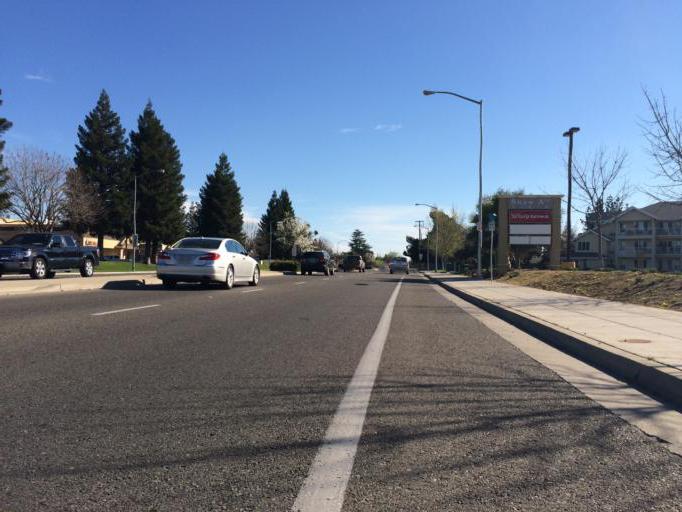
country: US
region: California
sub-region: Fresno County
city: Tarpey Village
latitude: 36.8082
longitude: -119.6821
